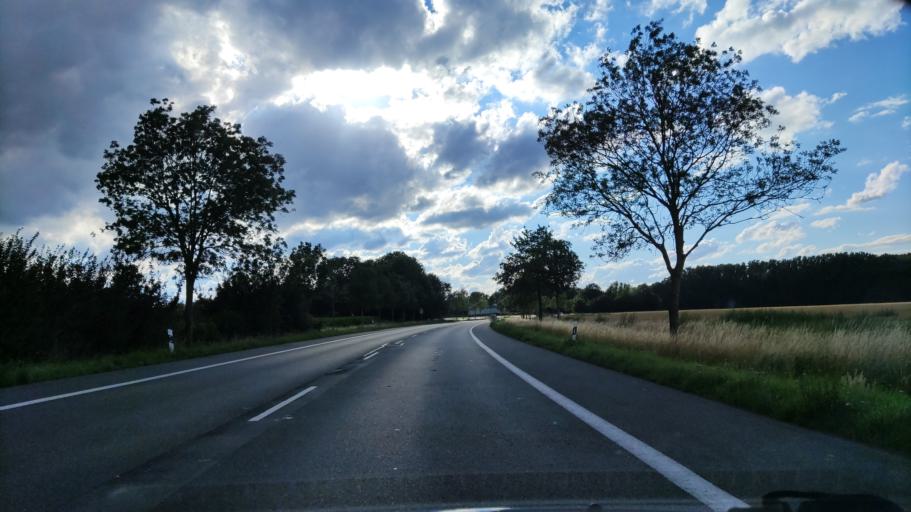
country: DE
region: North Rhine-Westphalia
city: Ahlen
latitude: 51.7721
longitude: 7.8544
